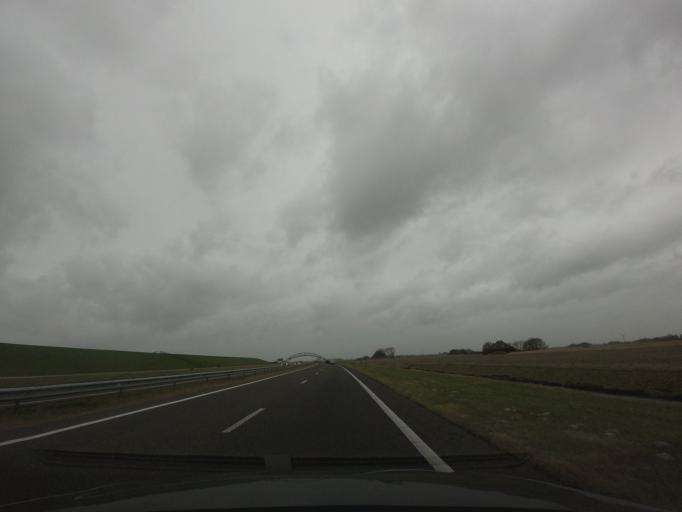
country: NL
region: Friesland
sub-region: Gemeente Harlingen
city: Harlingen
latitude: 53.1180
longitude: 5.4037
